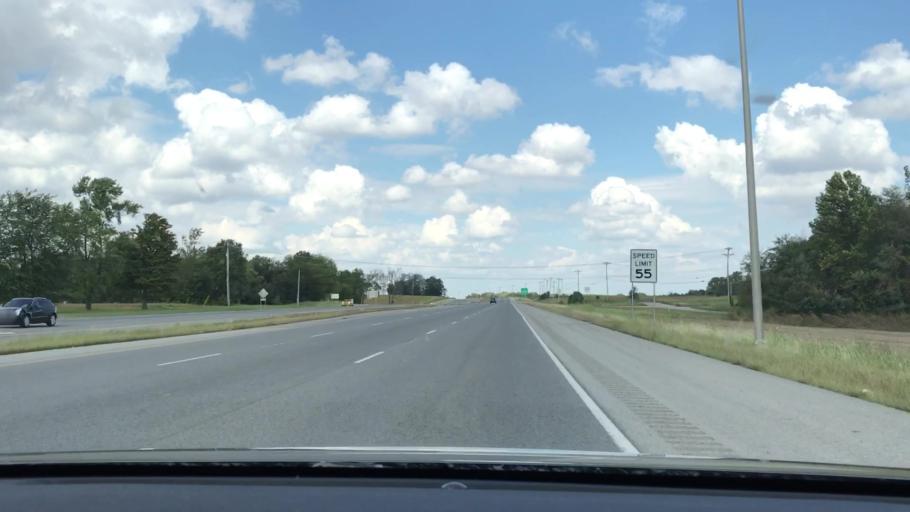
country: US
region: Kentucky
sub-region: Christian County
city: Oak Grove
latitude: 36.6771
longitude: -87.4466
